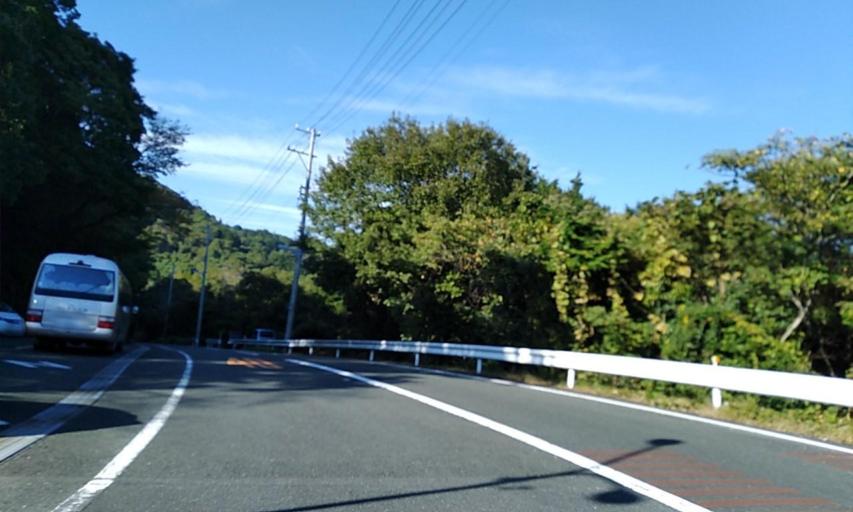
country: JP
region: Shizuoka
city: Hamakita
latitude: 34.8132
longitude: 137.6497
